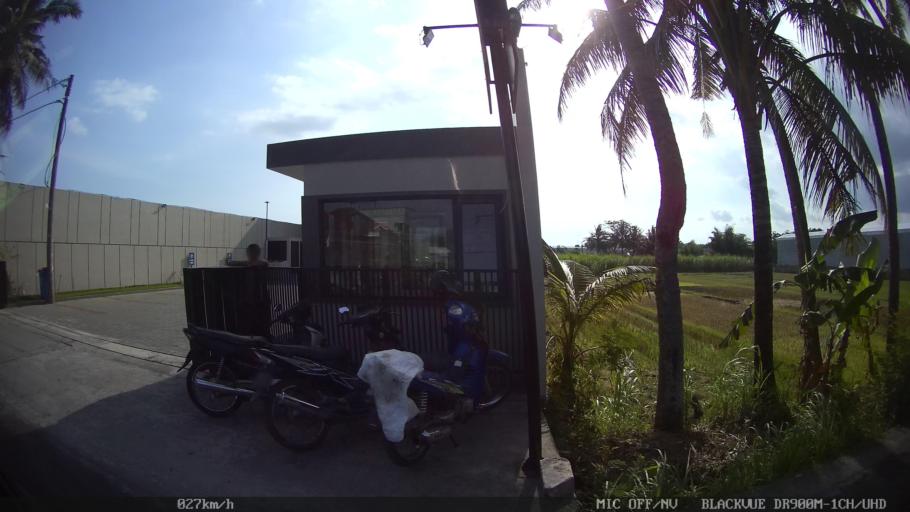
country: ID
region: Daerah Istimewa Yogyakarta
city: Kasihan
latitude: -7.8300
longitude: 110.3236
